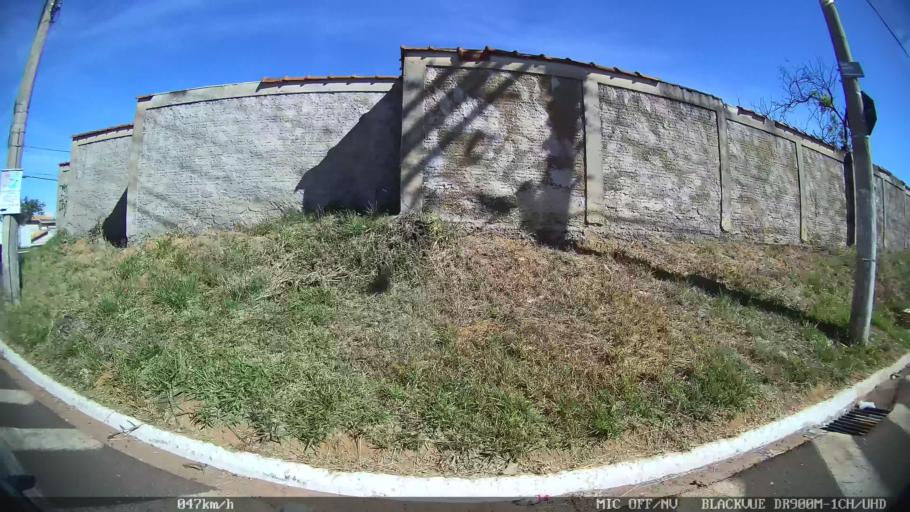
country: BR
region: Sao Paulo
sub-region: Franca
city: Franca
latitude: -20.5642
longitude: -47.3585
